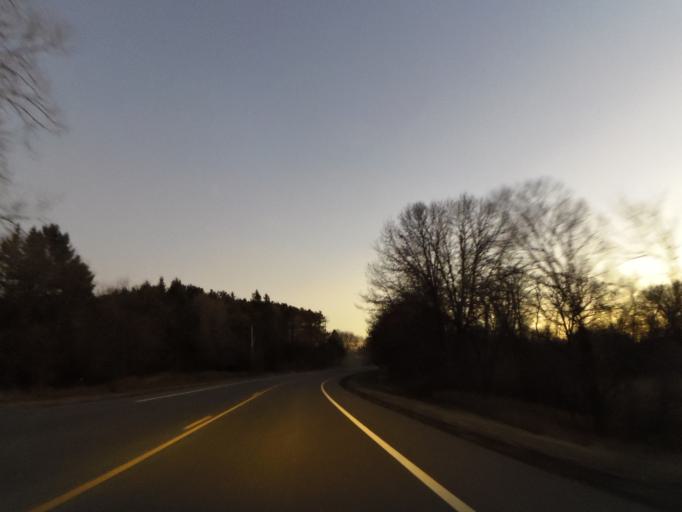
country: US
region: Minnesota
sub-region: Washington County
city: Stillwater
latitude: 45.1170
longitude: -92.8341
